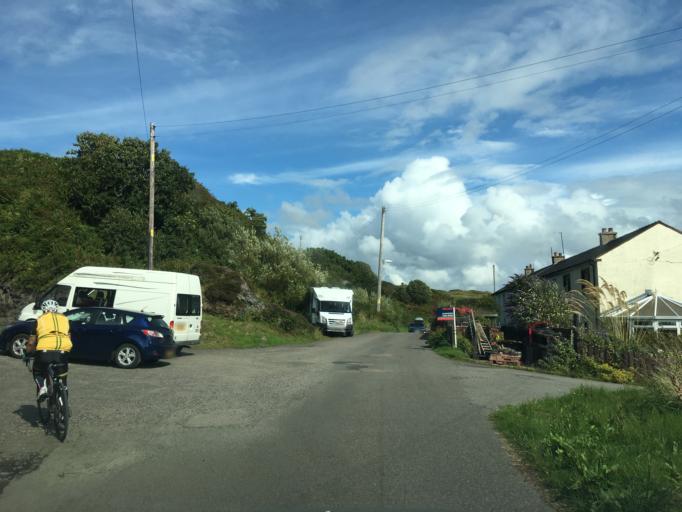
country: GB
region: Scotland
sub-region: Argyll and Bute
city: Isle Of Mull
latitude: 56.2491
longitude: -5.6503
